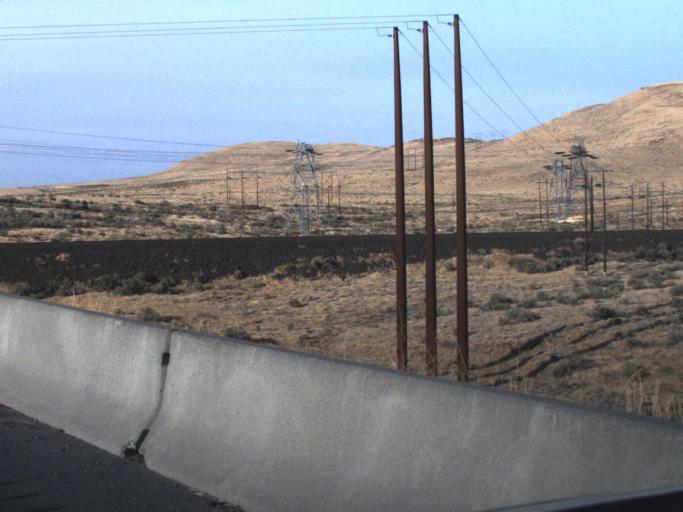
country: US
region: Oregon
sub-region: Umatilla County
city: Umatilla
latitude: 45.9369
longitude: -119.3310
